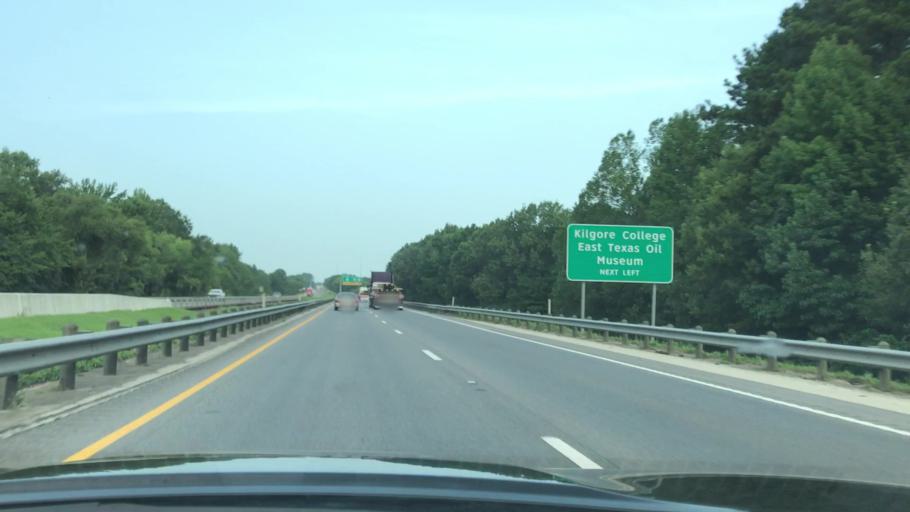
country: US
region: Texas
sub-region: Gregg County
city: Kilgore
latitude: 32.4351
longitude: -94.8143
